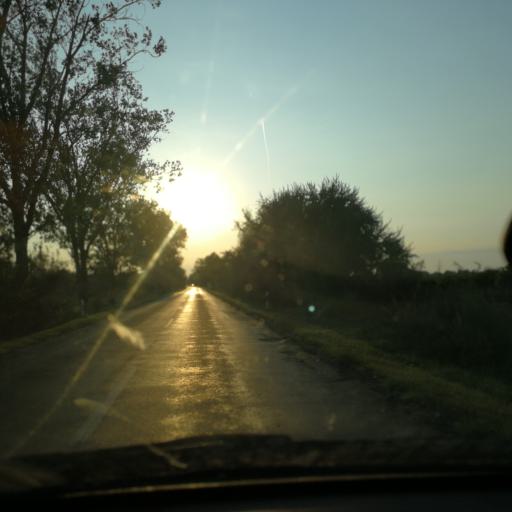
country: HU
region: Bacs-Kiskun
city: Kiskunhalas
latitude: 46.4297
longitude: 19.5222
